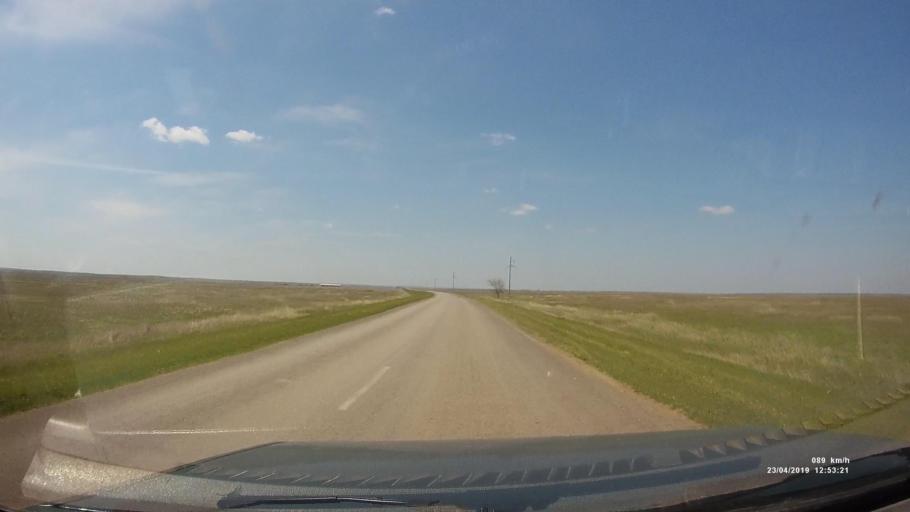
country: RU
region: Kalmykiya
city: Yashalta
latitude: 46.5733
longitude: 42.5973
